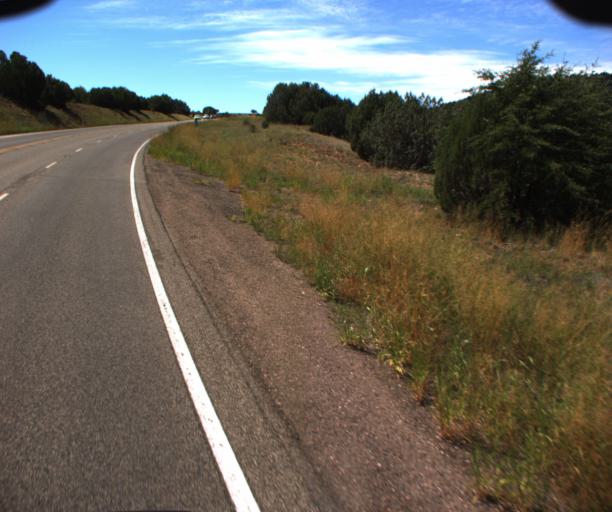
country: US
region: Arizona
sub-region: Navajo County
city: Cibecue
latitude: 33.7316
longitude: -110.5253
